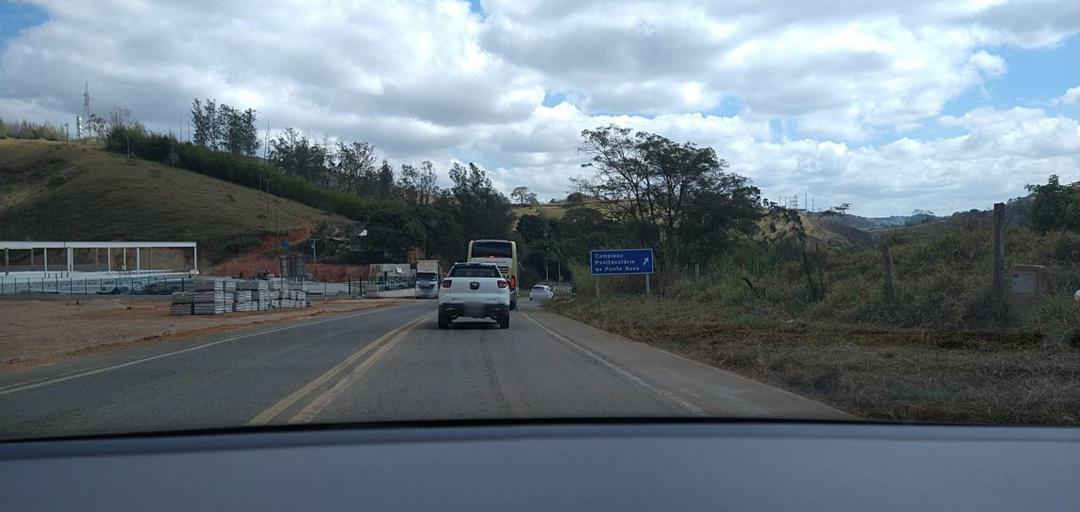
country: BR
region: Minas Gerais
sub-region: Ponte Nova
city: Ponte Nova
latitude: -20.4307
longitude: -42.8919
